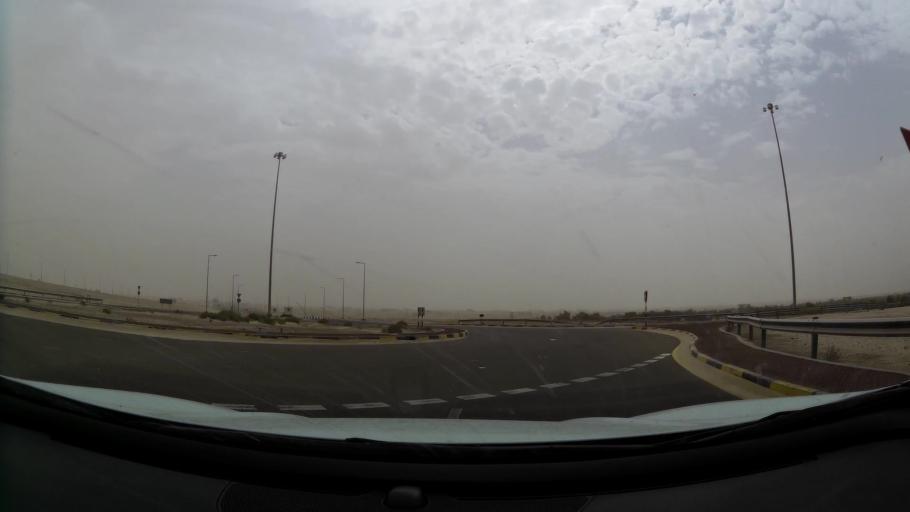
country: AE
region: Abu Dhabi
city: Abu Dhabi
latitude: 24.3756
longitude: 54.7347
